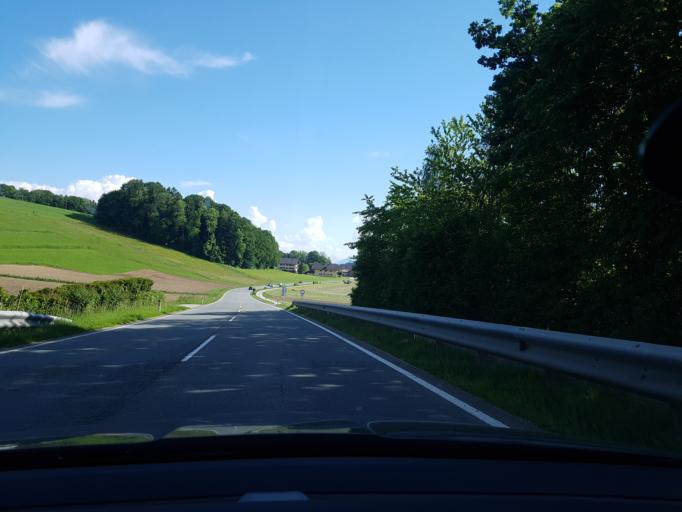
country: AT
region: Salzburg
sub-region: Politischer Bezirk Salzburg-Umgebung
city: Seeham
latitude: 47.9550
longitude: 13.0900
